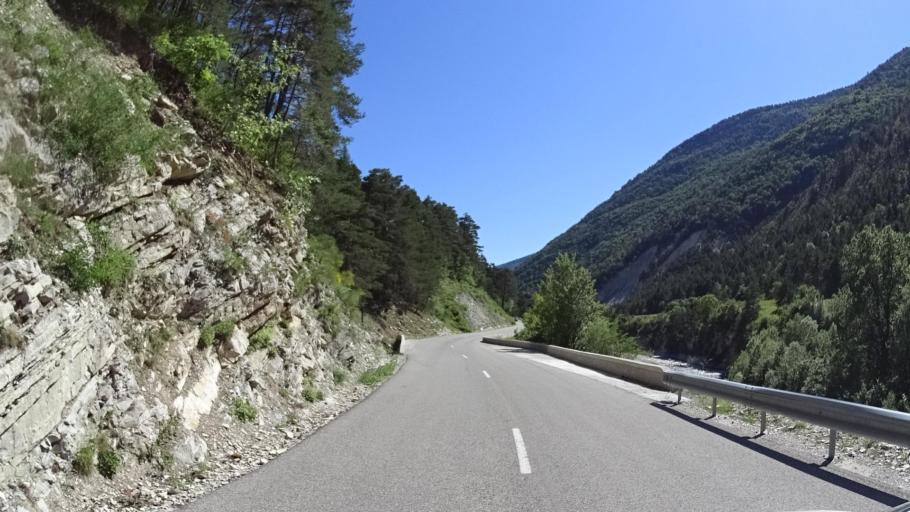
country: FR
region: Provence-Alpes-Cote d'Azur
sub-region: Departement des Alpes-de-Haute-Provence
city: Annot
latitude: 44.0486
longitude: 6.5689
